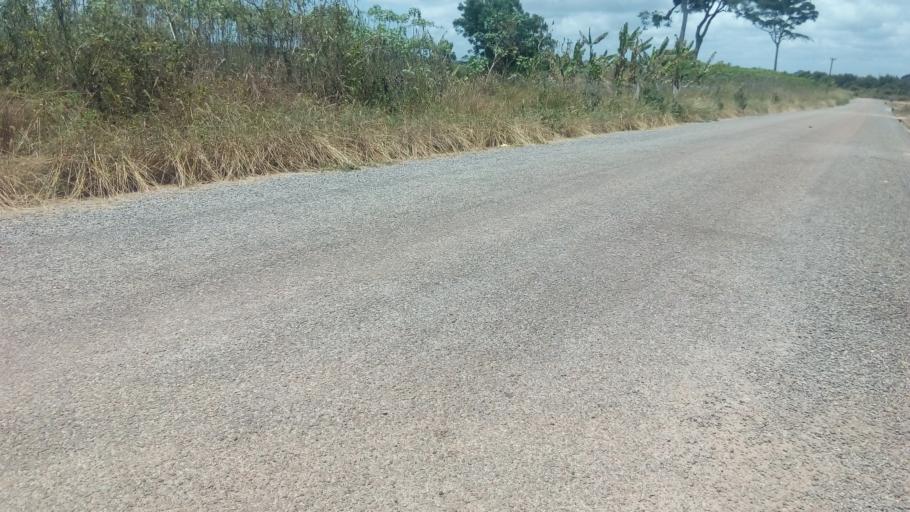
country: GH
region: Central
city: Cape Coast
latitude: 5.1330
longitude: -1.2943
